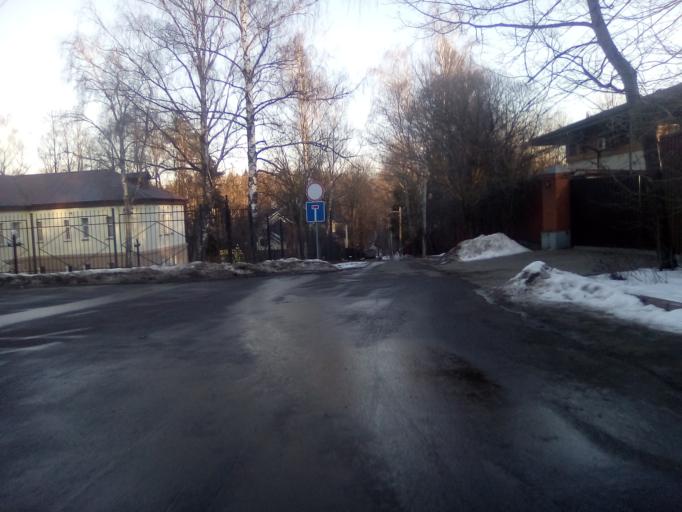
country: RU
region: Moskovskaya
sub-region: Leninskiy Rayon
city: Vnukovo
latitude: 55.6361
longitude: 37.2700
